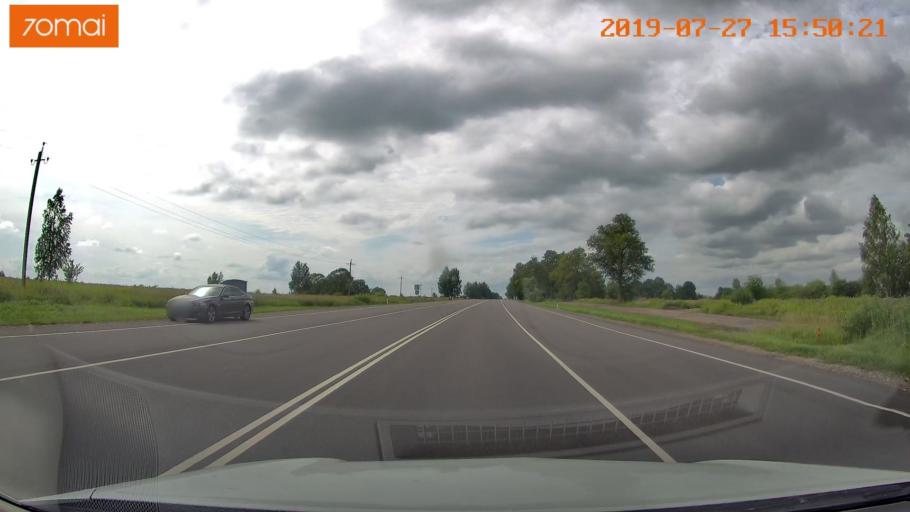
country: RU
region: Kaliningrad
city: Ozersk
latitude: 54.6004
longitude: 22.0096
